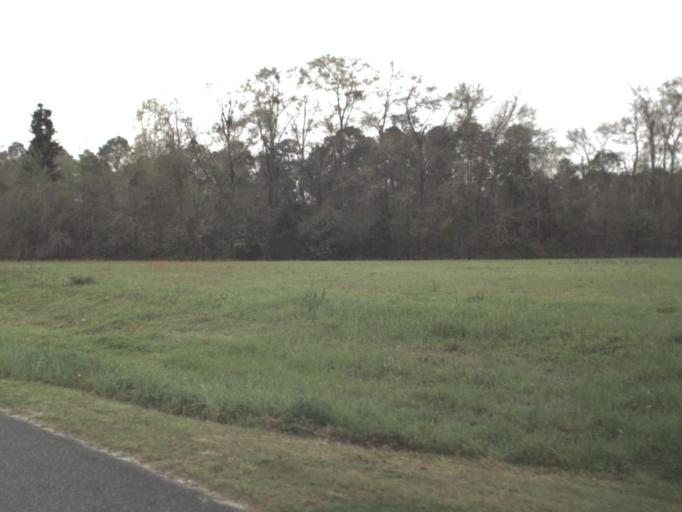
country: US
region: Florida
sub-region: Calhoun County
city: Blountstown
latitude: 30.4560
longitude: -85.1884
